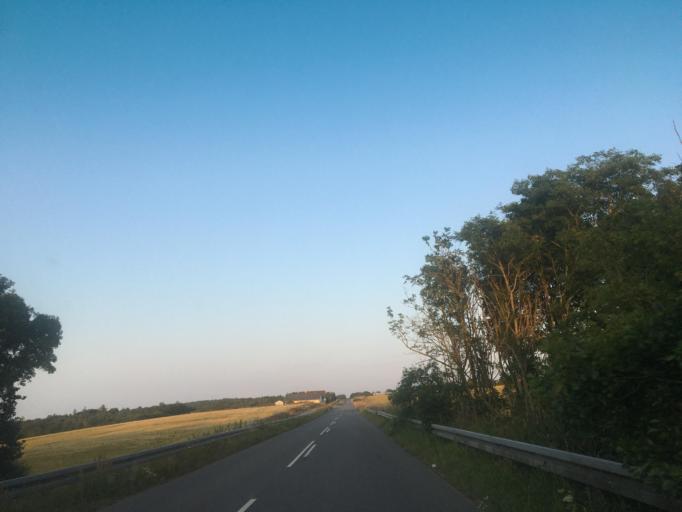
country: DK
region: North Denmark
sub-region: Thisted Kommune
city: Hurup
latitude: 56.7570
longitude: 8.3552
